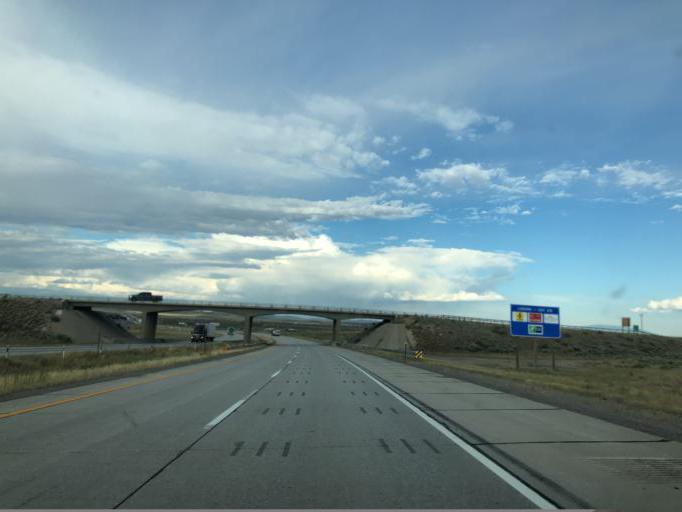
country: US
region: Wyoming
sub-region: Carbon County
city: Rawlins
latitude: 41.7779
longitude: -107.2265
